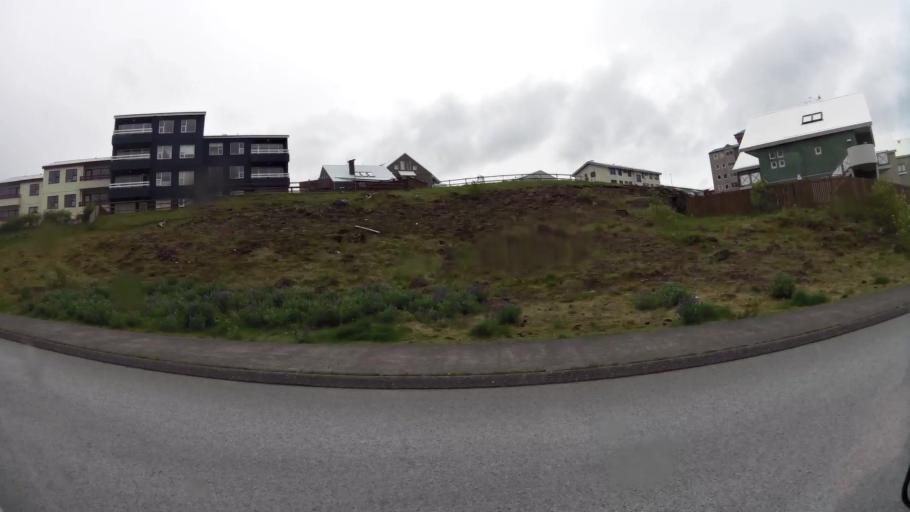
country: IS
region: Capital Region
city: Hafnarfjoerdur
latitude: 64.0576
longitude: -21.9803
